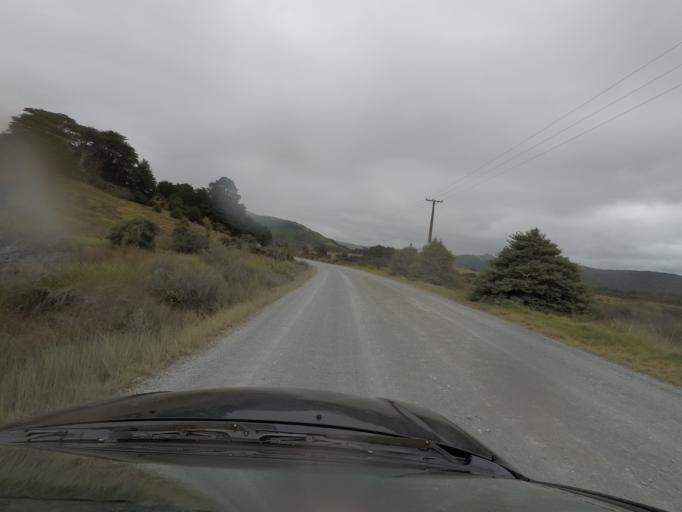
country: NZ
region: Auckland
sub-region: Auckland
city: Warkworth
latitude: -36.2506
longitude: 174.7189
